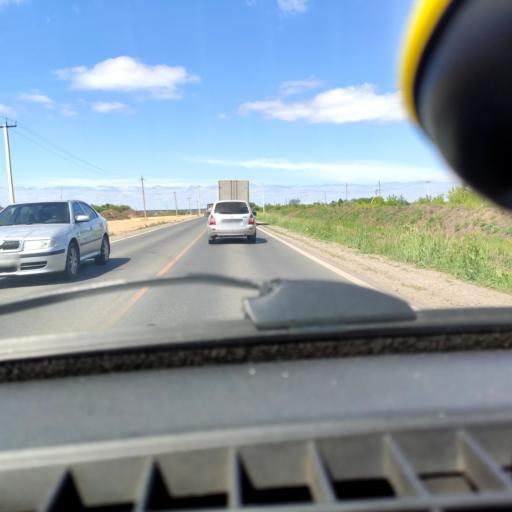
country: RU
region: Samara
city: Podstepki
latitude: 53.5643
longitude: 49.1603
